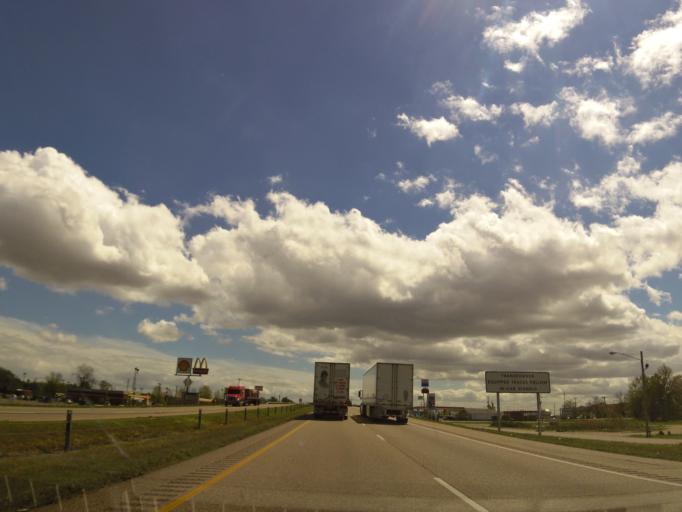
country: US
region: Arkansas
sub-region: Crittenden County
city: Marion
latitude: 35.2150
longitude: -90.2077
